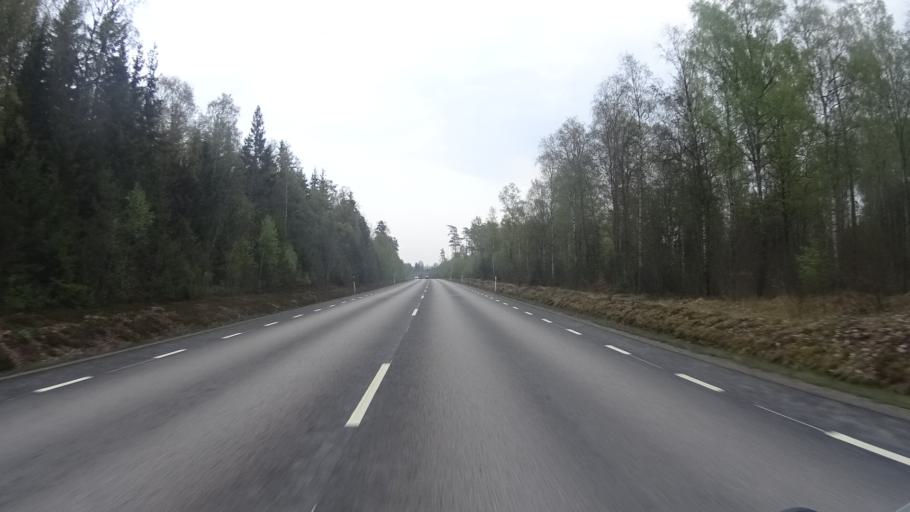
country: SE
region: Kronoberg
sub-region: Ljungby Kommun
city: Ljungby
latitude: 56.8232
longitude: 13.9586
